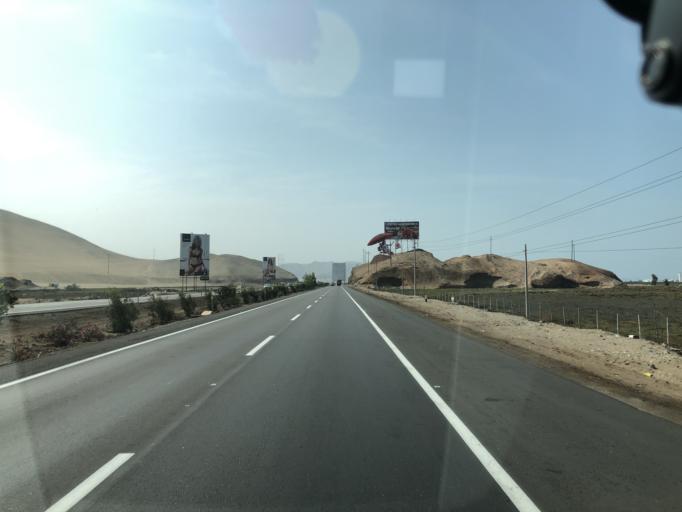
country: PE
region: Lima
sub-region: Provincia de Canete
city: Chilca
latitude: -12.5525
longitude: -76.7125
